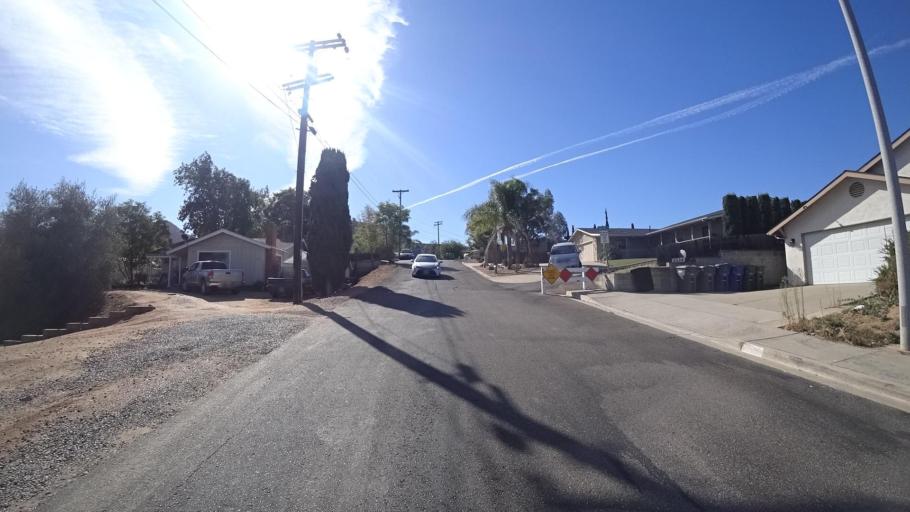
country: US
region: California
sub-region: San Diego County
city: Granite Hills
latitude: 32.8302
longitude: -116.9010
